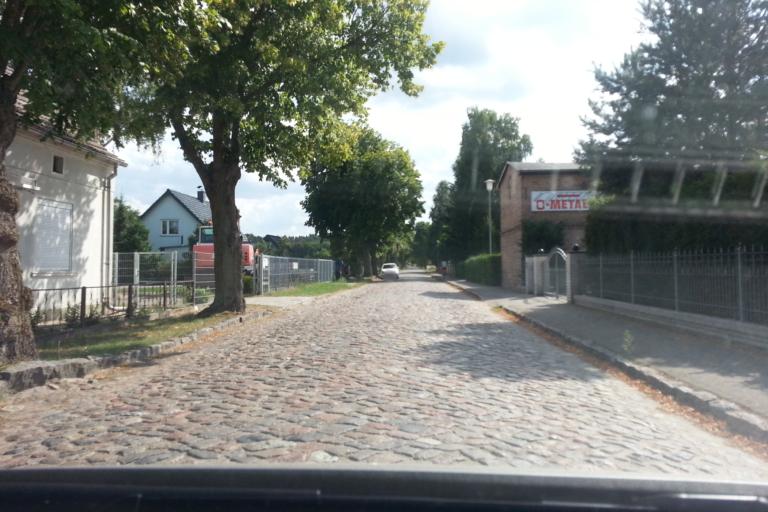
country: DE
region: Mecklenburg-Vorpommern
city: Ferdinandshof
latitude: 53.6347
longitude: 13.8688
